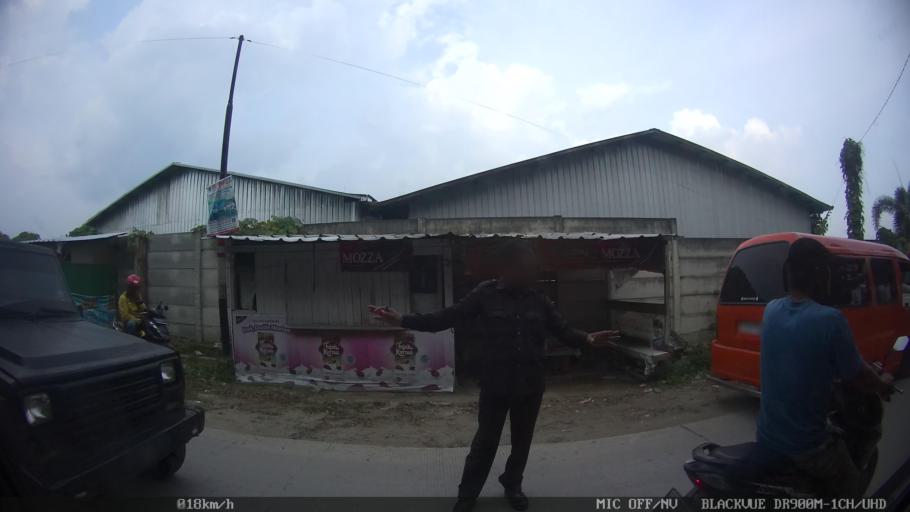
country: ID
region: Lampung
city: Bandarlampung
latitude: -5.4380
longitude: 105.2966
